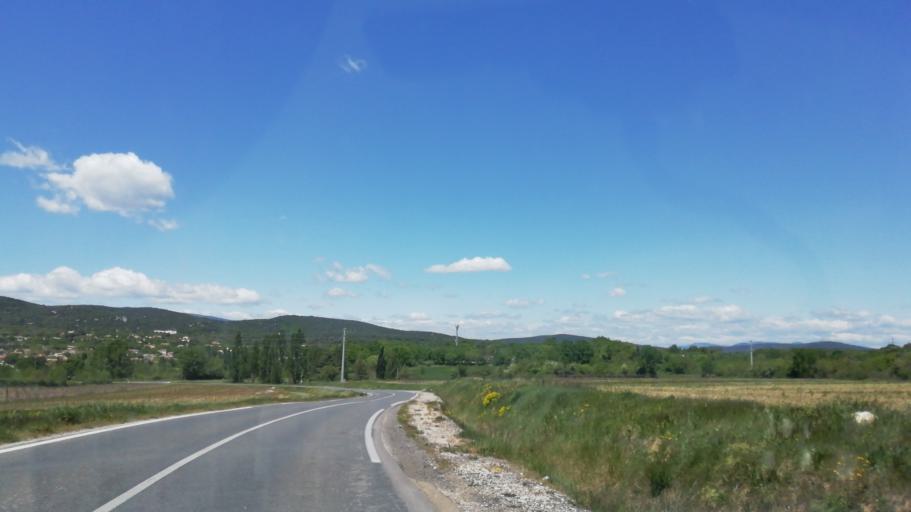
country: FR
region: Languedoc-Roussillon
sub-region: Departement de l'Herault
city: Saint-Martin-de-Londres
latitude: 43.7874
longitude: 3.7405
